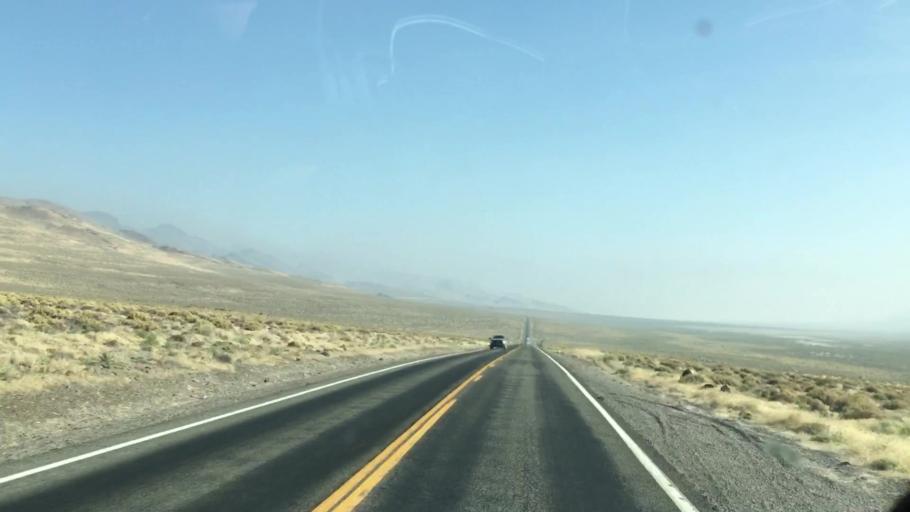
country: US
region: Nevada
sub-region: Lyon County
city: Fernley
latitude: 39.9591
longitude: -119.3837
